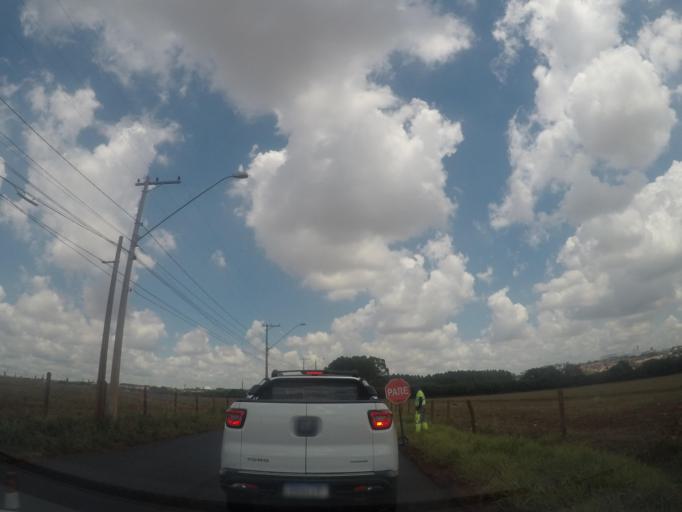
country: BR
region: Sao Paulo
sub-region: Hortolandia
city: Hortolandia
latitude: -22.8214
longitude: -47.2253
